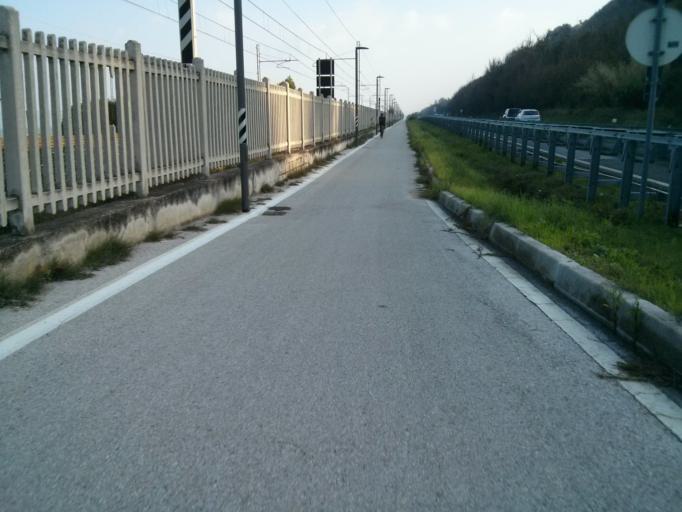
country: IT
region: The Marches
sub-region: Provincia di Pesaro e Urbino
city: Fenile
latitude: 43.8781
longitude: 12.9663
